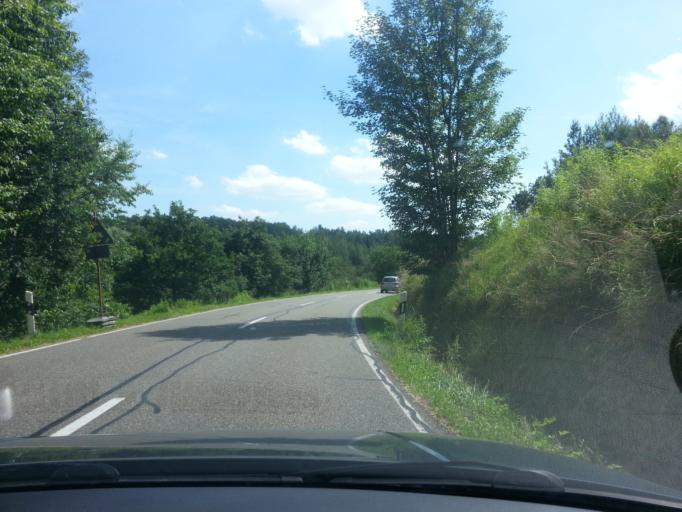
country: DE
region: Saarland
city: Spiesen-Elversberg
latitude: 49.2970
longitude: 7.1603
